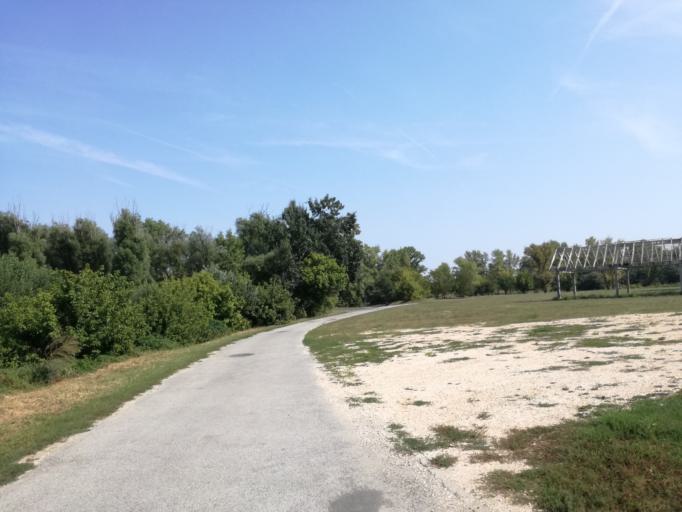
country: HU
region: Pest
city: Szazhalombatta
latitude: 47.3503
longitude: 18.9422
